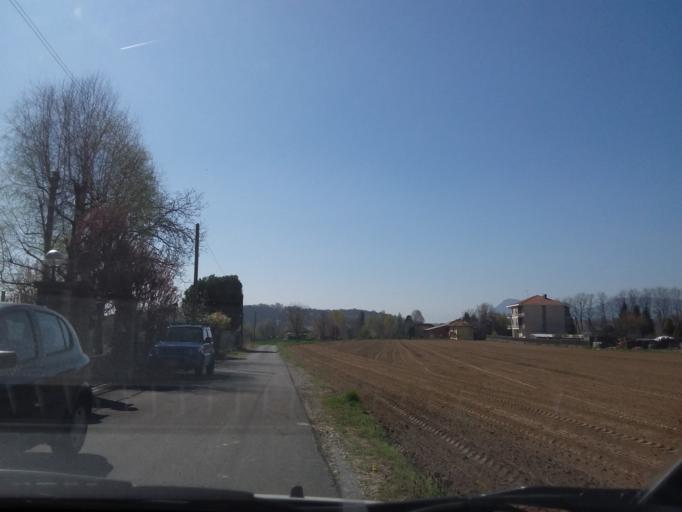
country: IT
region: Piedmont
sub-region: Provincia di Torino
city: Rivoli
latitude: 45.0606
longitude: 7.5072
